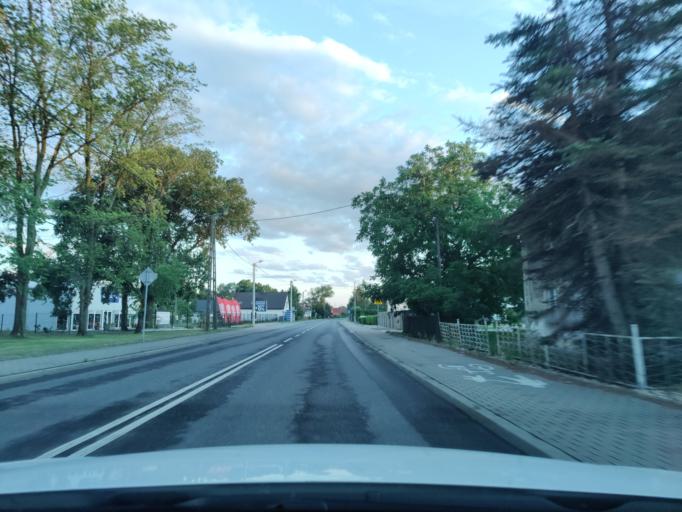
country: PL
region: Opole Voivodeship
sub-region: Powiat nyski
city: Chroscina
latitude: 50.6562
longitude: 17.3883
